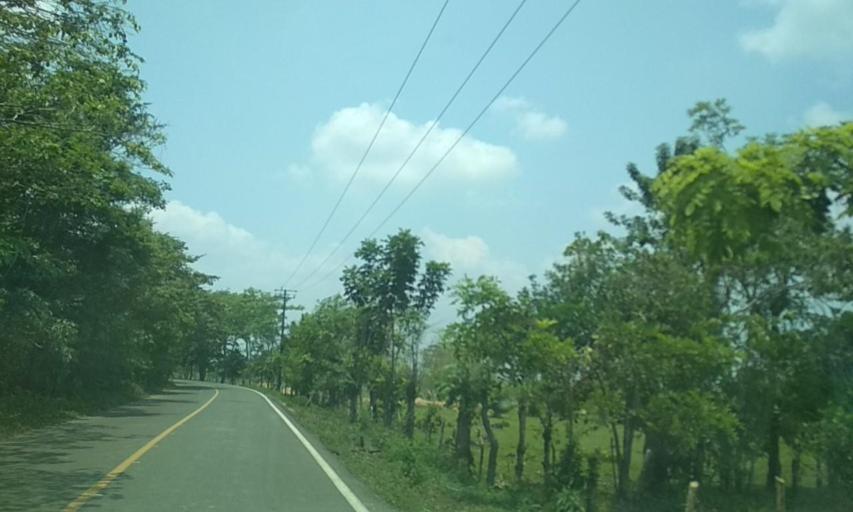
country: MX
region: Tabasco
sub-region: Huimanguillo
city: Francisco Rueda
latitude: 17.7598
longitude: -94.0099
